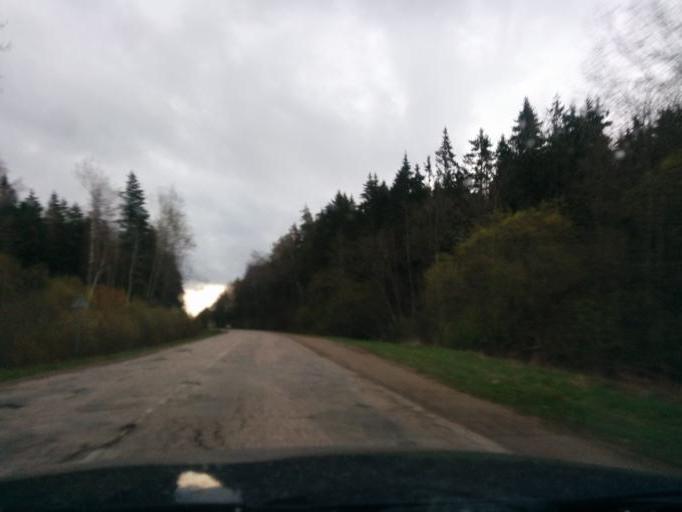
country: LT
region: Siauliu apskritis
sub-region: Joniskis
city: Joniskis
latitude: 56.4160
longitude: 23.6242
